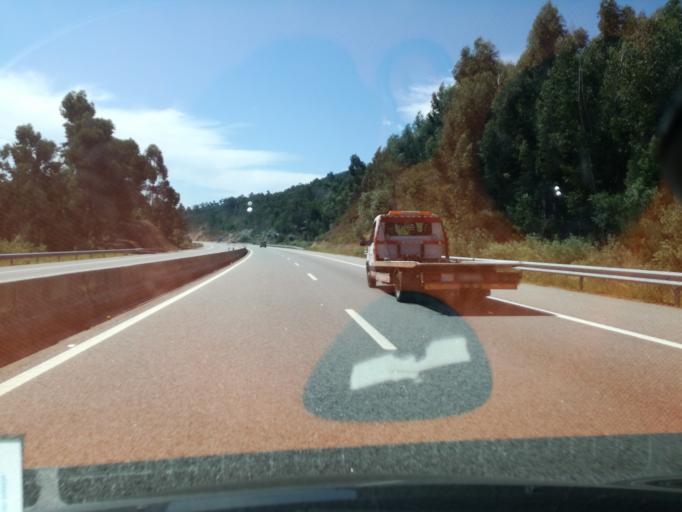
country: PT
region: Viana do Castelo
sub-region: Viana do Castelo
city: Meadela
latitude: 41.7648
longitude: -8.7924
